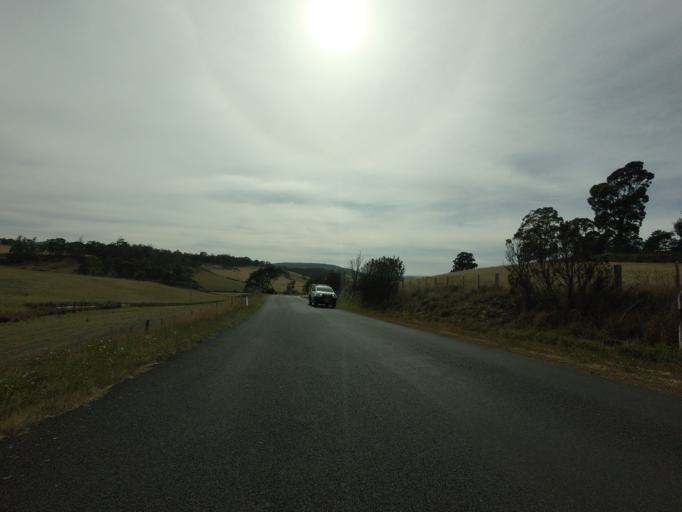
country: AU
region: Tasmania
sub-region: Sorell
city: Sorell
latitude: -42.4277
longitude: 147.4972
